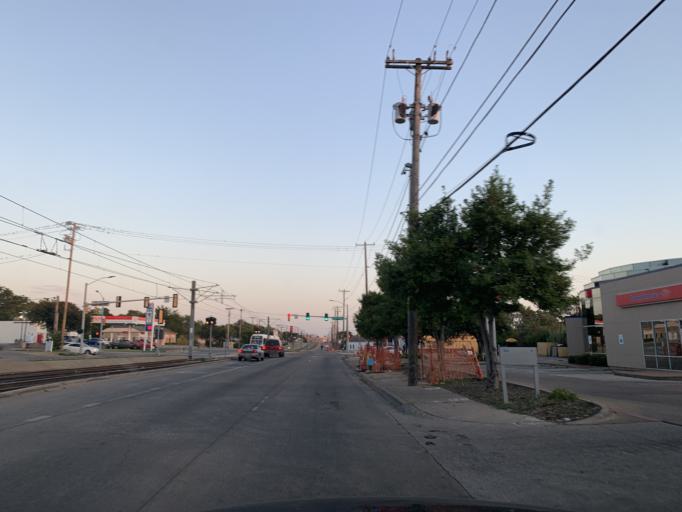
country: US
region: Texas
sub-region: Dallas County
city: Dallas
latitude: 32.7052
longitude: -96.7999
